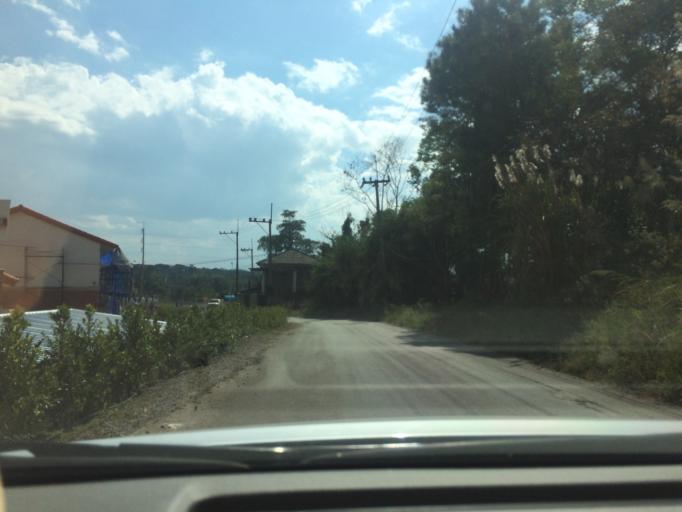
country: TH
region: Phetchabun
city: Khao Kho
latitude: 16.7705
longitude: 101.0388
